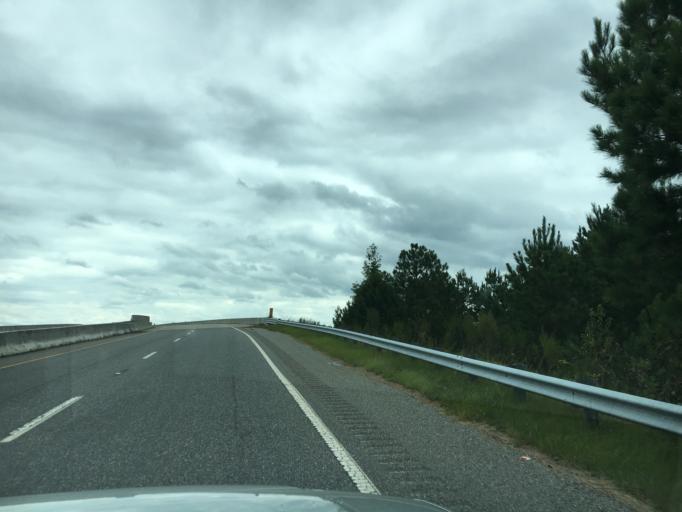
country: US
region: South Carolina
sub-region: Greenville County
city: Mauldin
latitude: 34.7546
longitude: -82.2897
